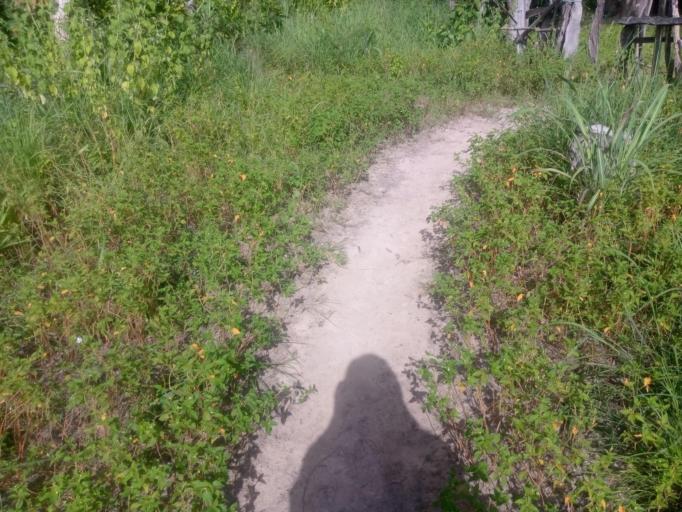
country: GM
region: Western
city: Gunjur
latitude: 13.0293
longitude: -16.7272
